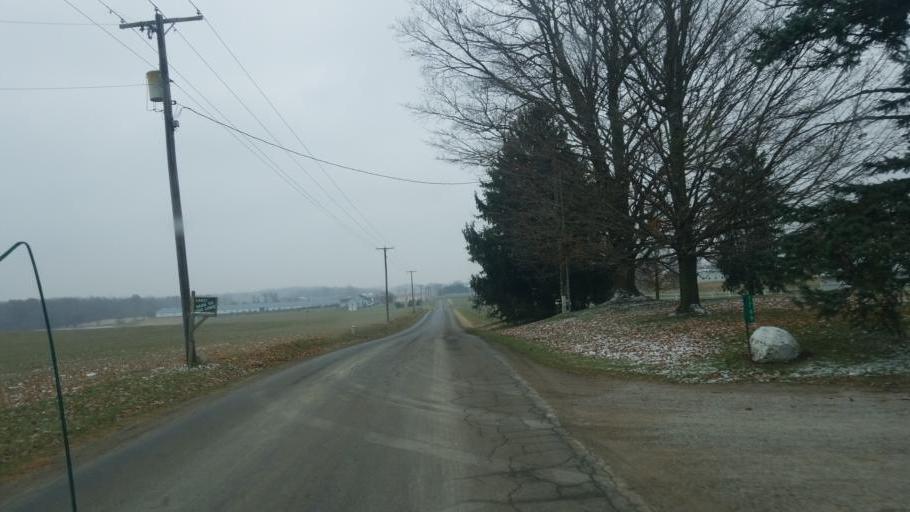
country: US
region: Ohio
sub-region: Huron County
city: Greenwich
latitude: 40.9748
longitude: -82.5788
